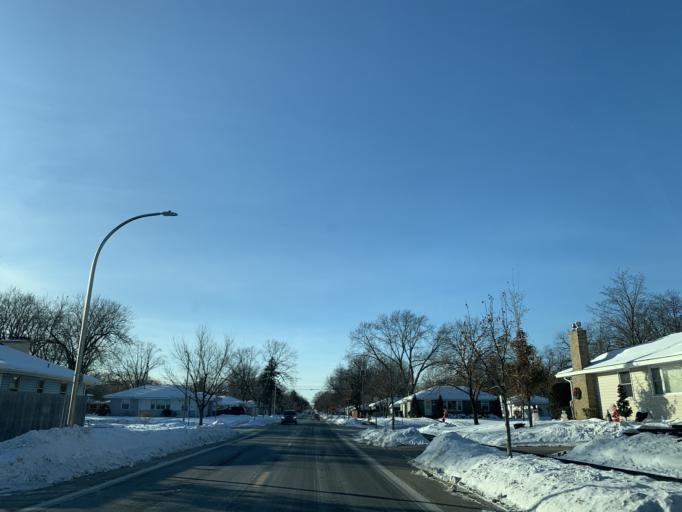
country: US
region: Minnesota
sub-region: Hennepin County
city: Richfield
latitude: 44.8656
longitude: -93.2523
